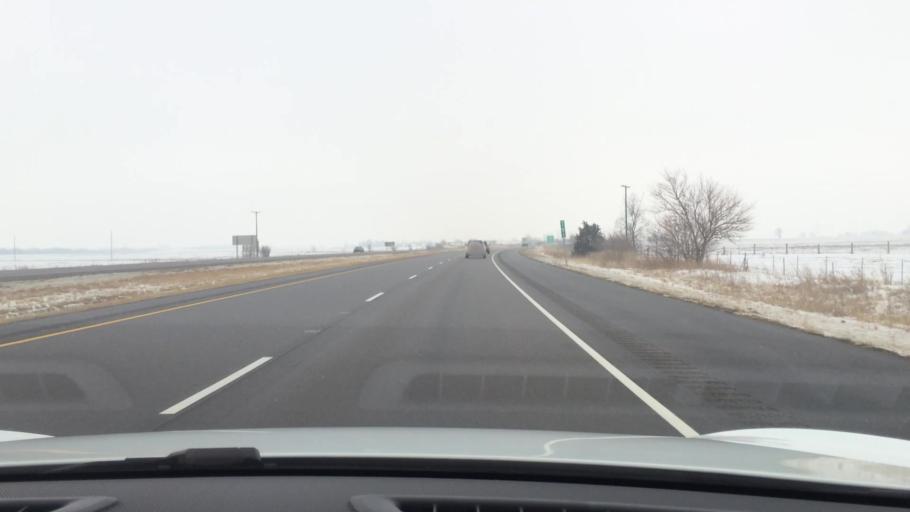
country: US
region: Illinois
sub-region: McLean County
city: Le Roy
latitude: 40.3236
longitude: -88.7407
